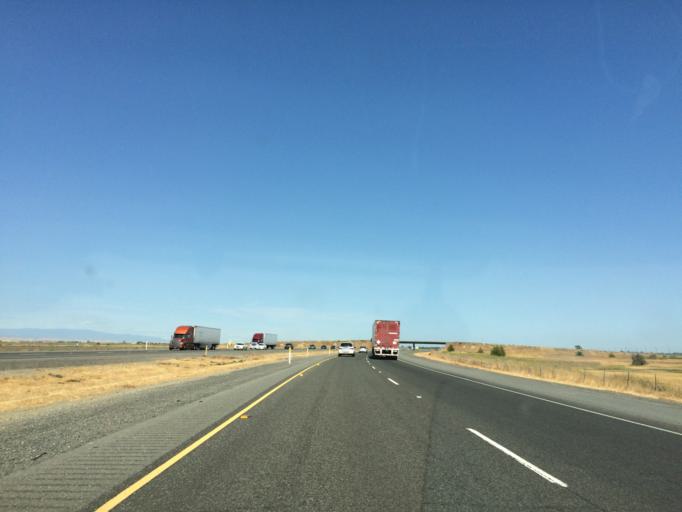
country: US
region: California
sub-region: Glenn County
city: Willows
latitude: 39.4611
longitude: -122.1949
